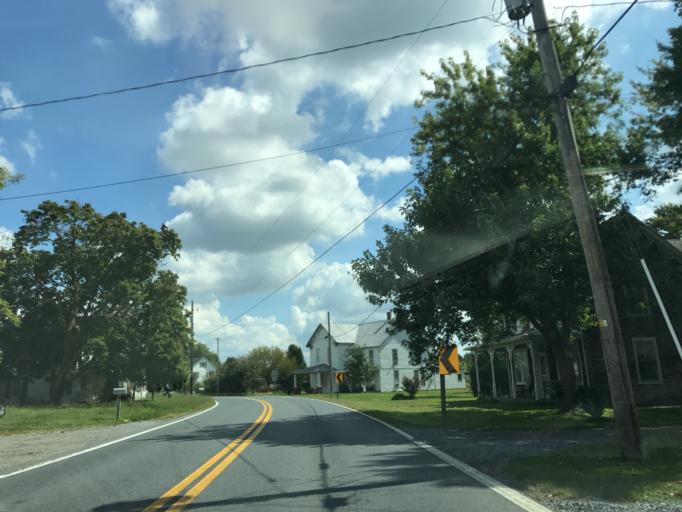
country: US
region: Maryland
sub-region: Caroline County
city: Ridgely
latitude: 39.0034
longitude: -75.9594
